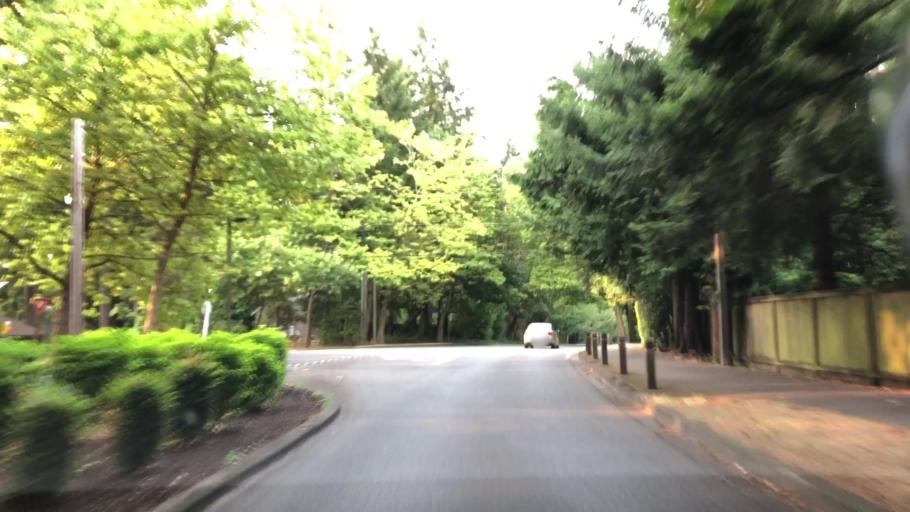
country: US
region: Washington
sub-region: King County
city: Mercer Island
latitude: 47.5551
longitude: -122.2215
